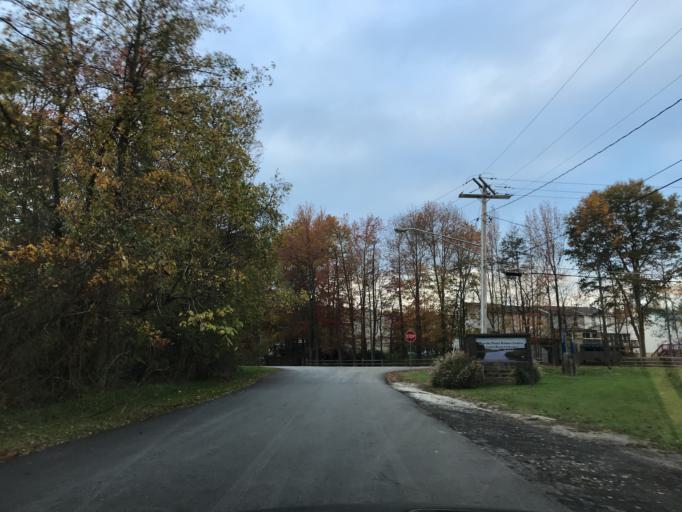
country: US
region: Maryland
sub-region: Baltimore County
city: Bowleys Quarters
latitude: 39.3502
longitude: -76.3782
